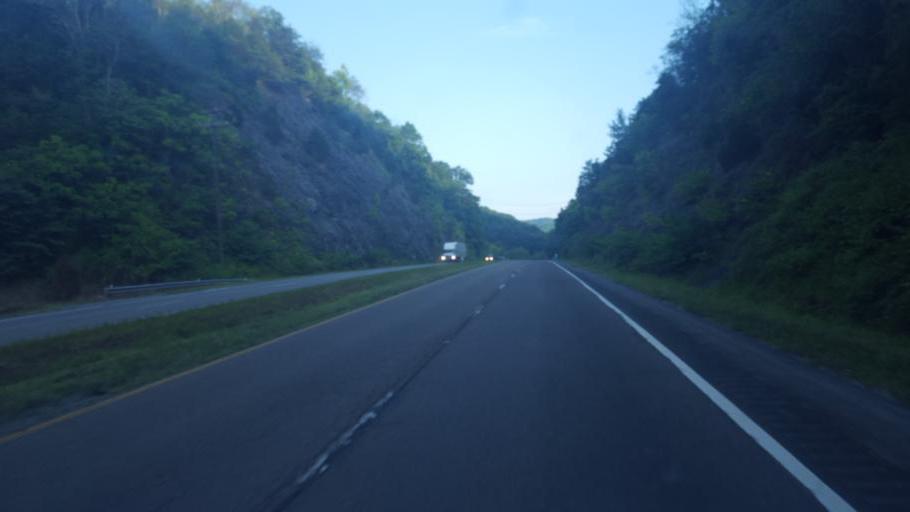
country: US
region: Tennessee
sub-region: Hawkins County
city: Church Hill
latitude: 36.6726
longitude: -82.7553
